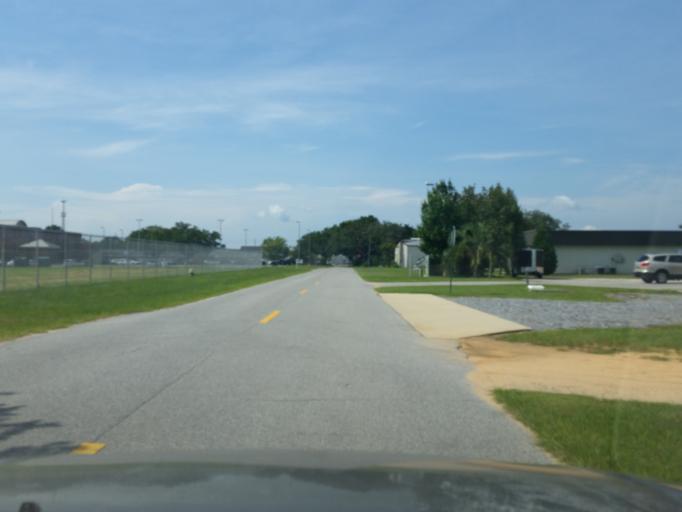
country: US
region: Florida
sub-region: Escambia County
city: Ferry Pass
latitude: 30.5320
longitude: -87.2002
